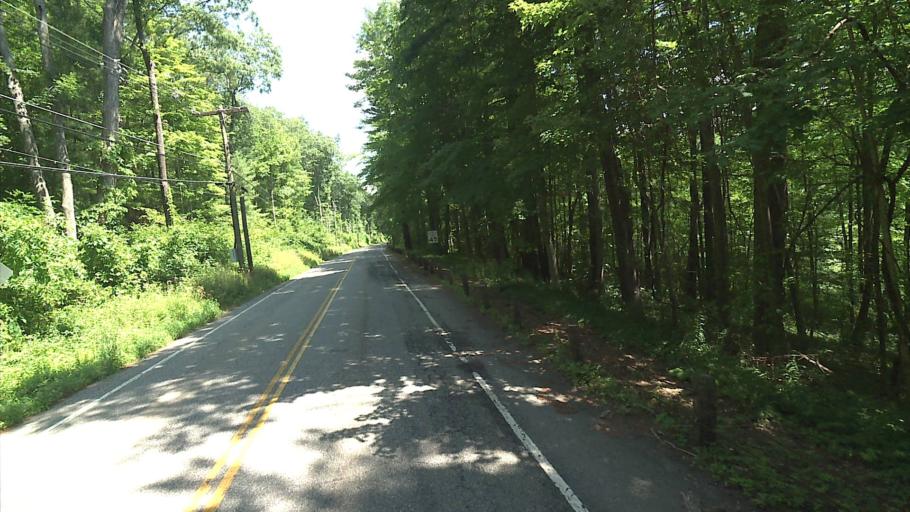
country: US
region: Connecticut
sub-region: Litchfield County
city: Litchfield
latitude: 41.8493
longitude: -73.3107
